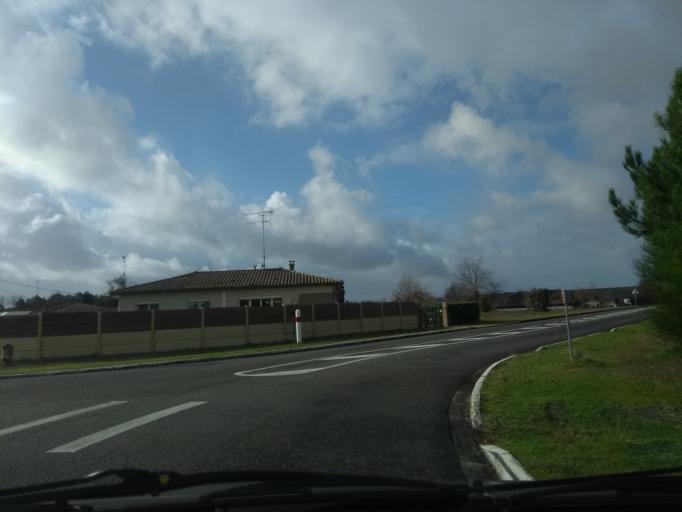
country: FR
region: Aquitaine
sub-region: Departement de la Gironde
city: Belin-Beliet
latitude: 44.4882
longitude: -0.7834
